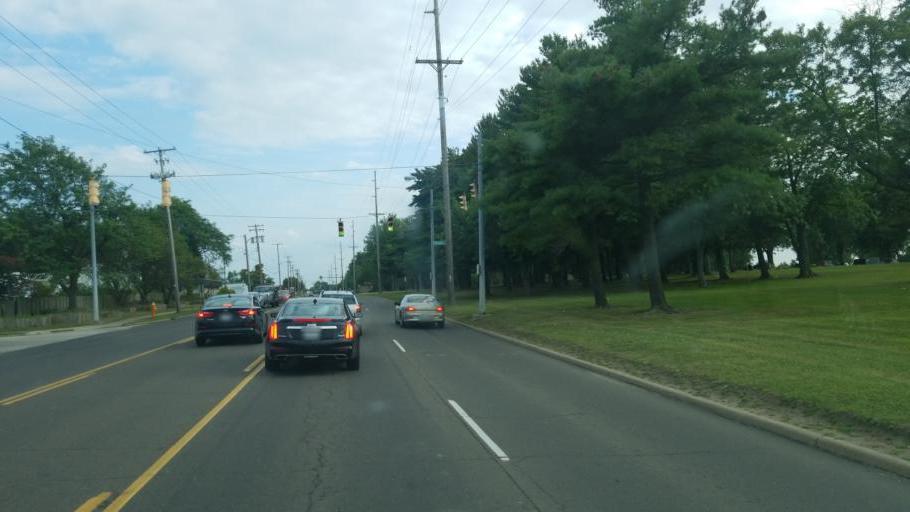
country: US
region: Ohio
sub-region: Trumbull County
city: Churchill
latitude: 41.1314
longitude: -80.6653
